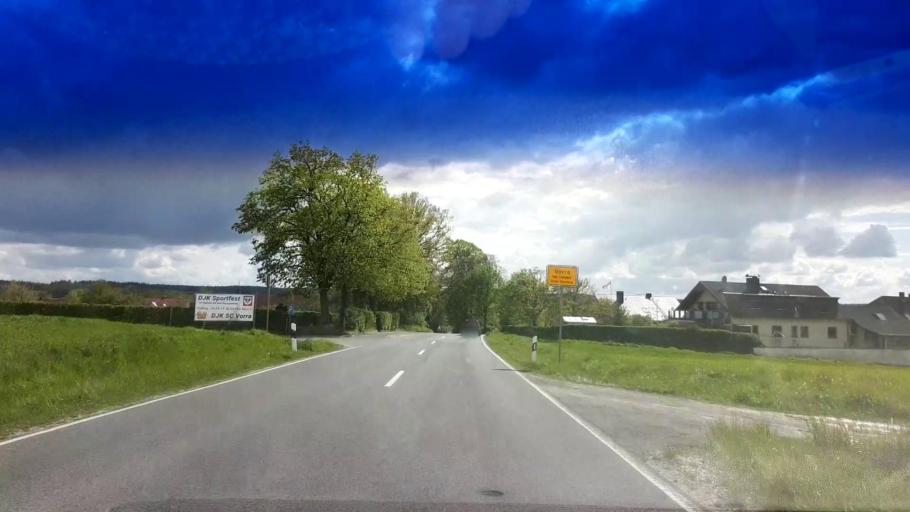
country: DE
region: Bavaria
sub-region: Upper Franconia
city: Frensdorf
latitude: 49.8272
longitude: 10.8413
